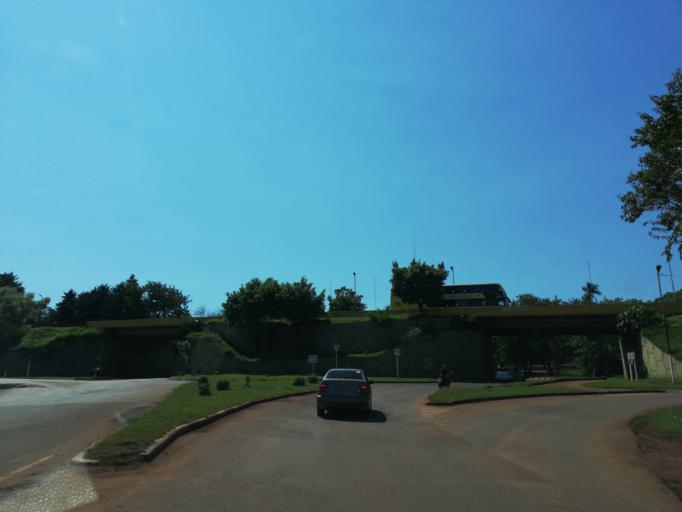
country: AR
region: Misiones
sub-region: Departamento de Eldorado
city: Eldorado
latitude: -26.4030
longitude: -54.6355
